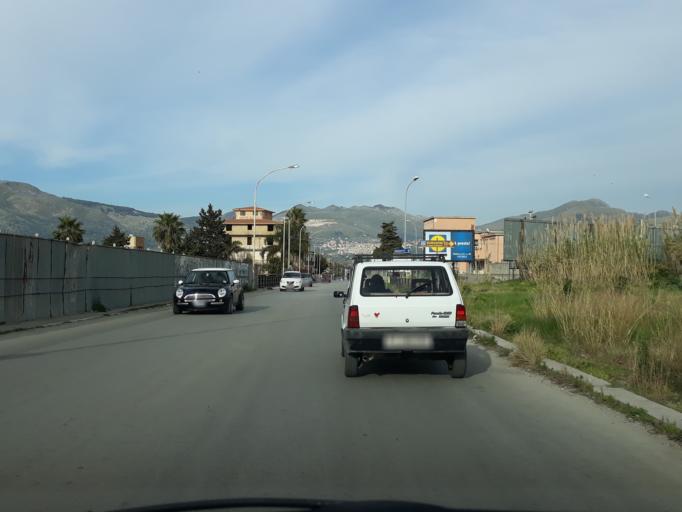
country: IT
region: Sicily
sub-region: Palermo
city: Partinico
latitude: 38.0532
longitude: 13.1270
